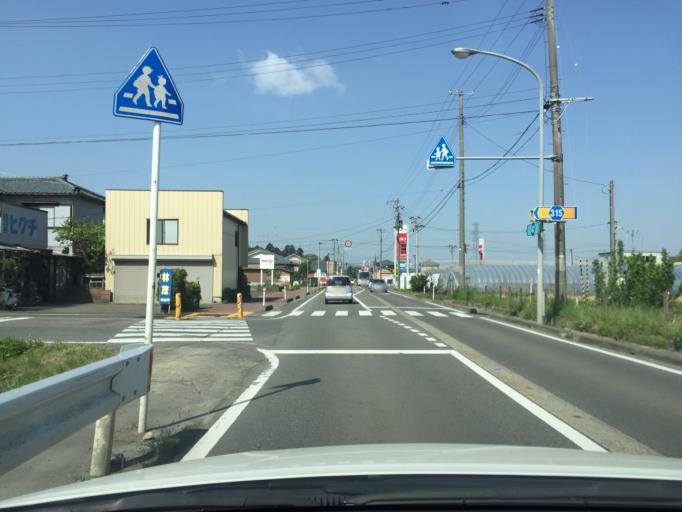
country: JP
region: Niigata
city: Gosen
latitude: 37.7479
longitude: 139.2054
